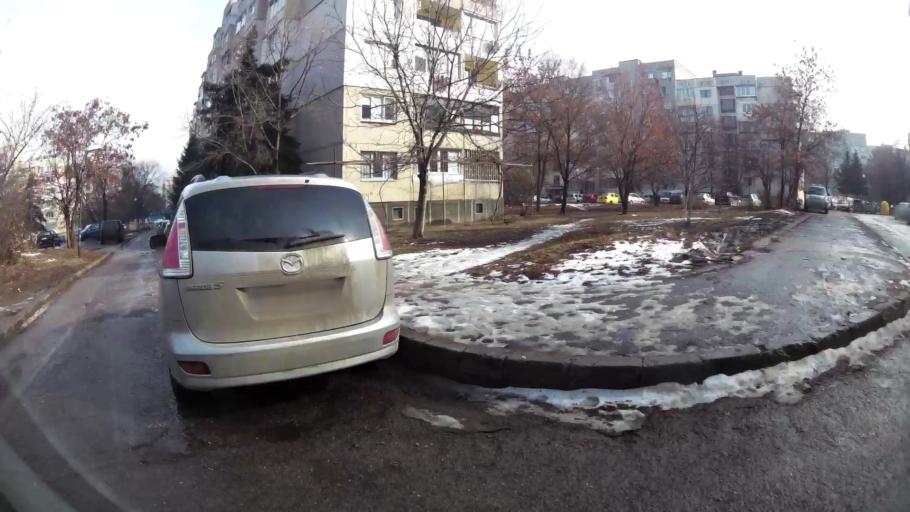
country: BG
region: Sofia-Capital
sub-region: Stolichna Obshtina
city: Sofia
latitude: 42.7175
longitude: 23.2633
